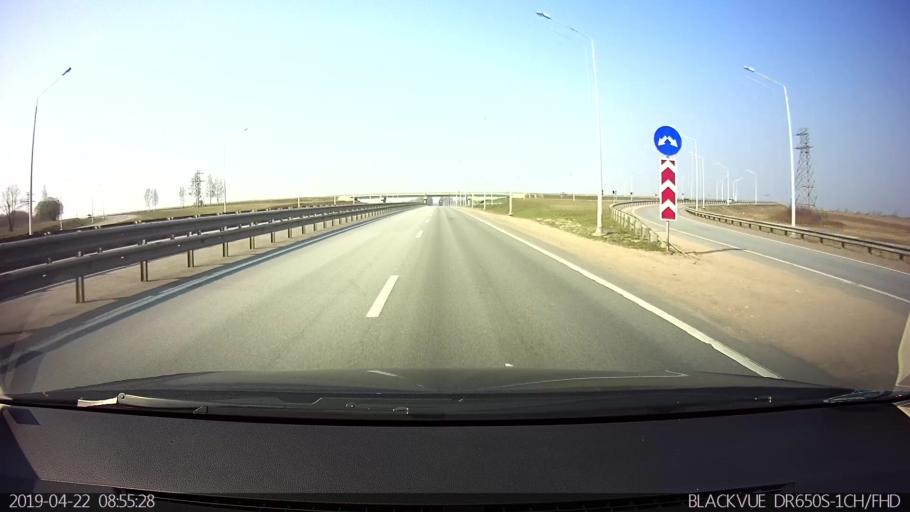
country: RU
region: Smolensk
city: Pechersk
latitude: 54.8818
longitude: 32.0652
